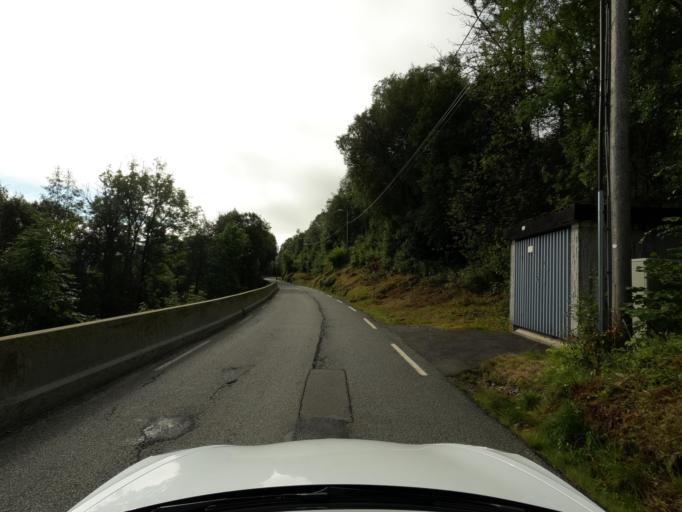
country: NO
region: Hordaland
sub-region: Bergen
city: Indre Arna
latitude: 60.4377
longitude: 5.4867
